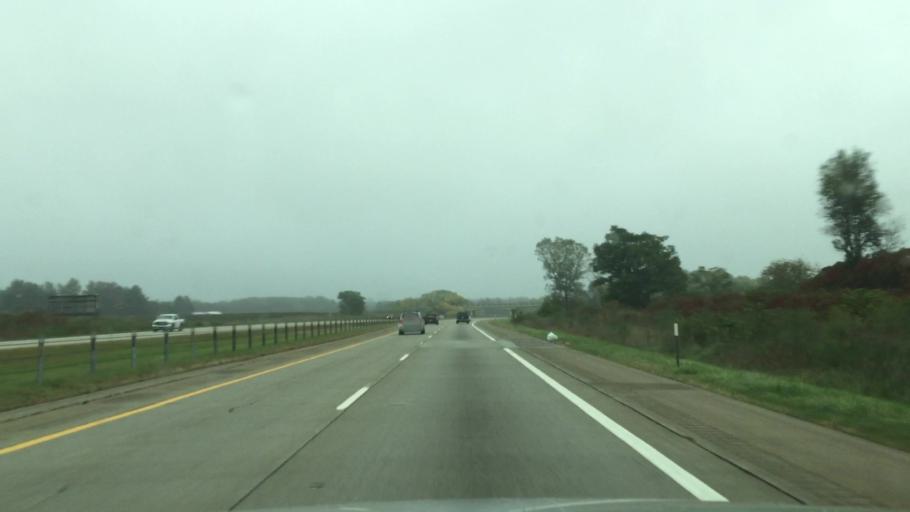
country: US
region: Michigan
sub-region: Van Buren County
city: Paw Paw
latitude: 42.2032
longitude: -85.9523
